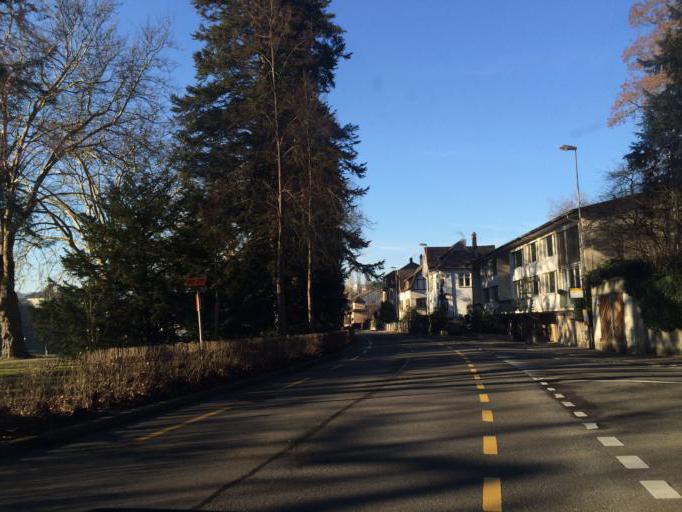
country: CH
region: Zurich
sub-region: Bezirk Andelfingen
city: Feuerthalen
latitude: 47.6922
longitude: 8.6521
